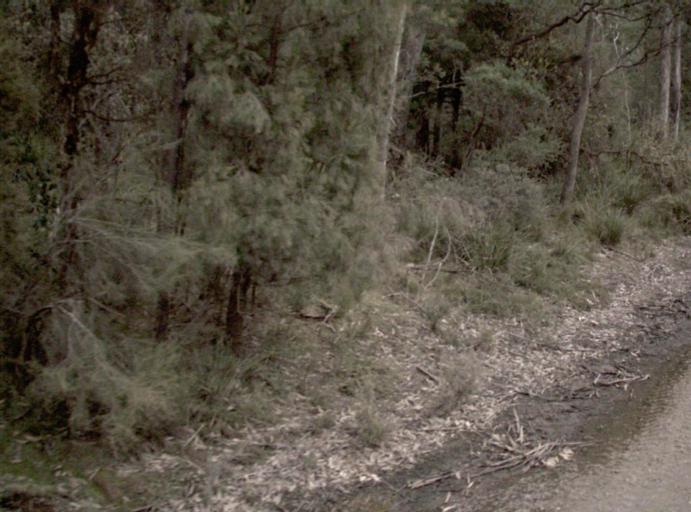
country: AU
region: Tasmania
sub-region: Launceston
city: Mayfield
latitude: -41.3515
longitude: 147.2200
